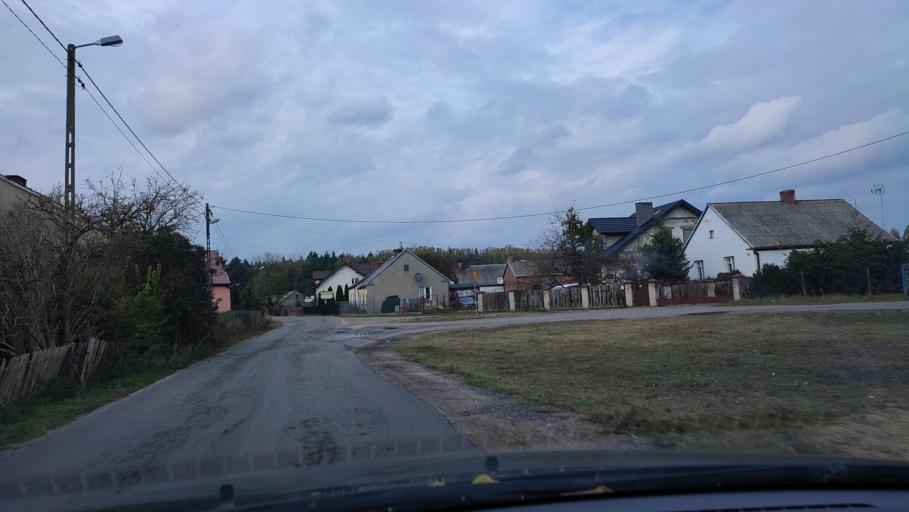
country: PL
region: Masovian Voivodeship
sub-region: Powiat mlawski
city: Mlawa
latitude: 53.1722
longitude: 20.3639
